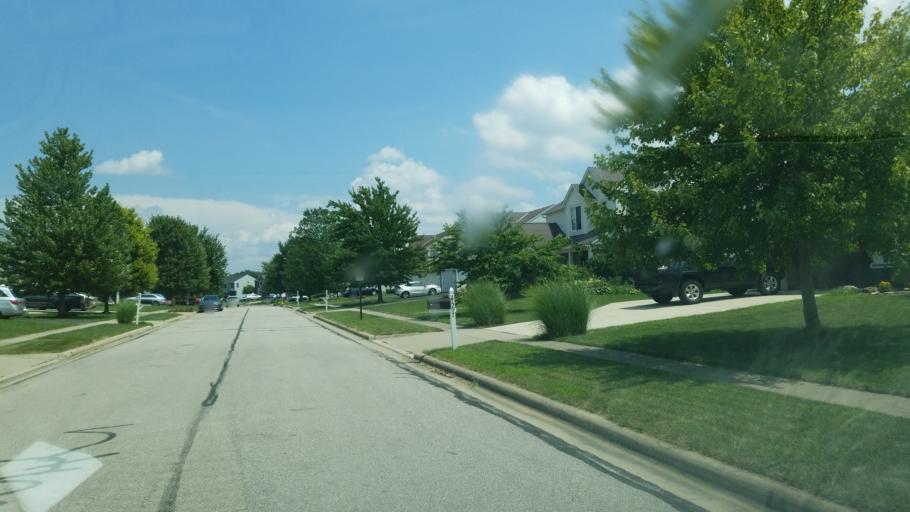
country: US
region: Ohio
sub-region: Delaware County
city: Lewis Center
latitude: 40.2176
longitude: -82.9983
